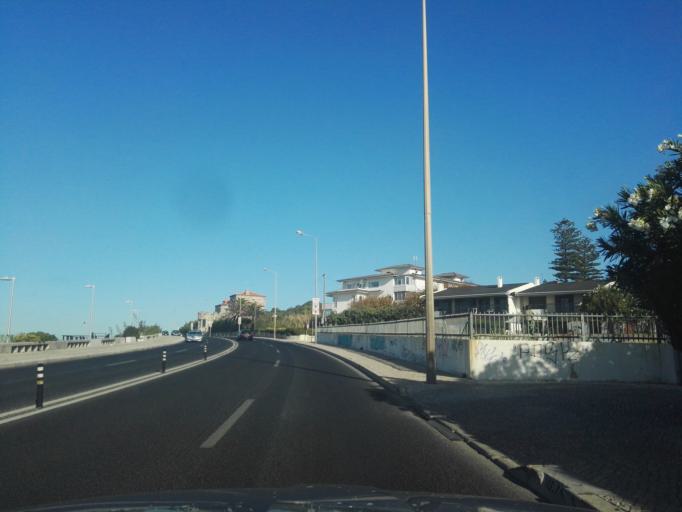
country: PT
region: Lisbon
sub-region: Cascais
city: Parede
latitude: 38.6882
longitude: -9.3597
